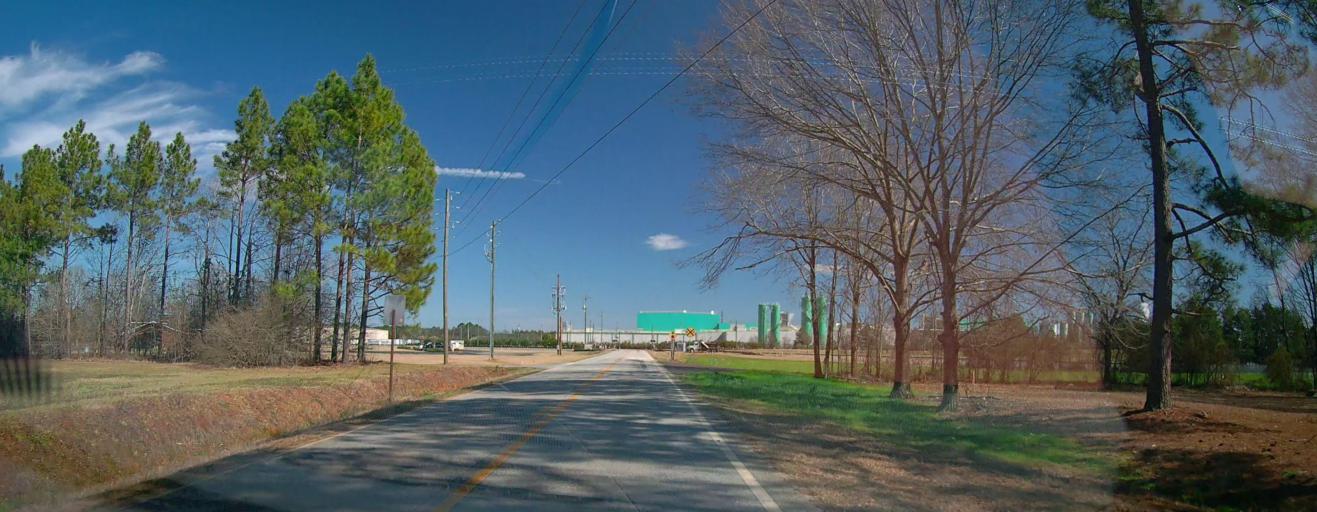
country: US
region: Georgia
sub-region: Houston County
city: Perry
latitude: 32.4854
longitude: -83.6154
